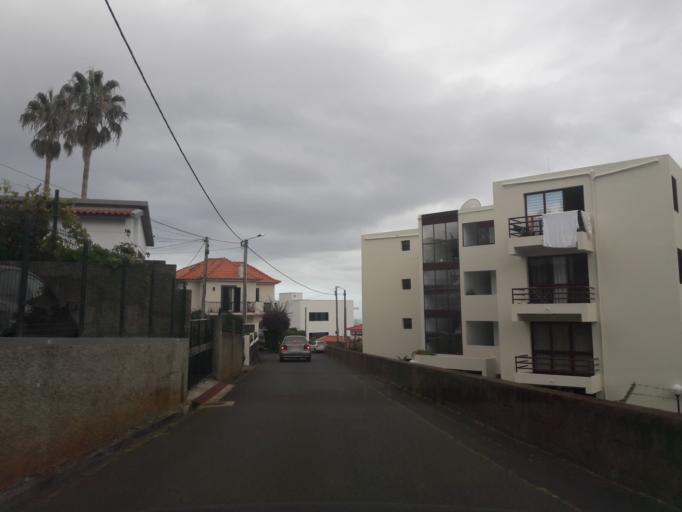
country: PT
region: Madeira
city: Canico
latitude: 32.6439
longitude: -16.8510
